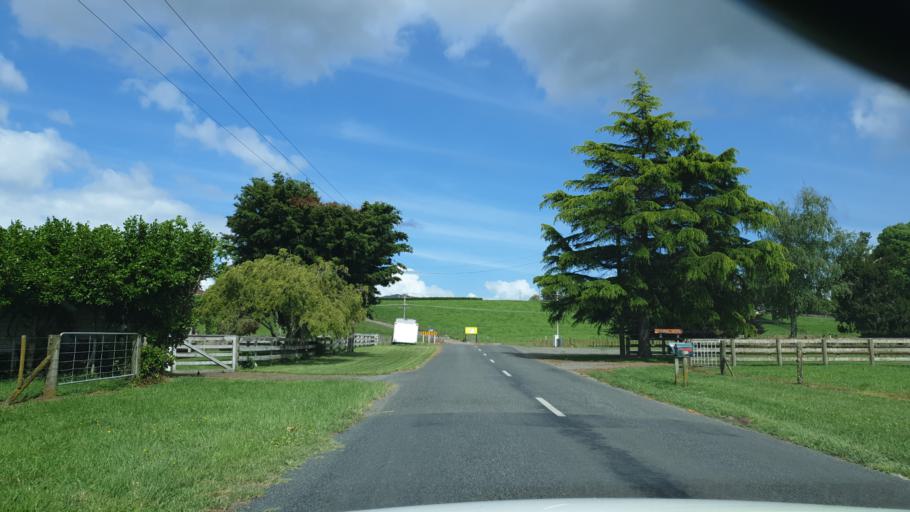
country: NZ
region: Waikato
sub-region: Matamata-Piako District
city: Matamata
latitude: -37.8295
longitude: 175.7281
